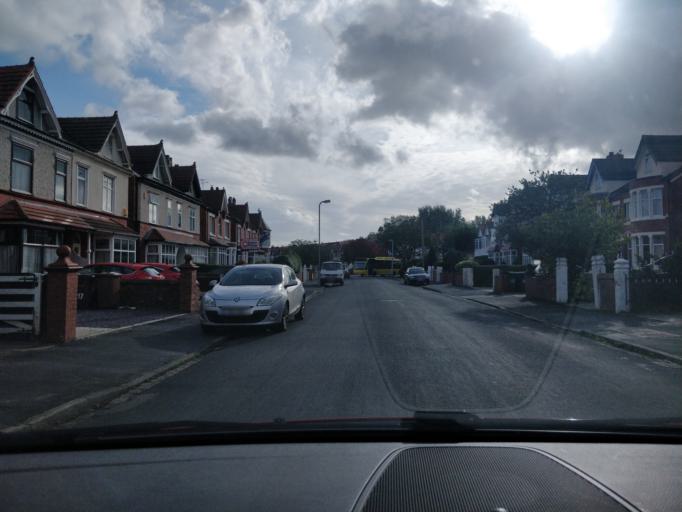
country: GB
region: England
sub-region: Sefton
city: Southport
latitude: 53.6232
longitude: -3.0170
